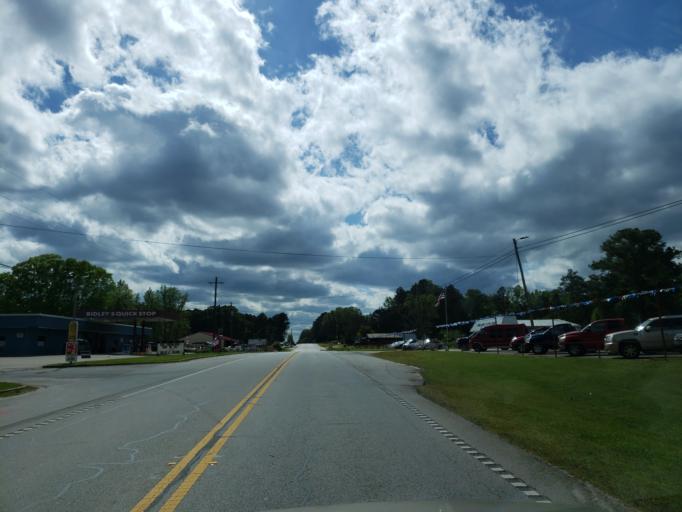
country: US
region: Georgia
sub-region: Haralson County
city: Tallapoosa
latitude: 33.7422
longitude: -85.3145
